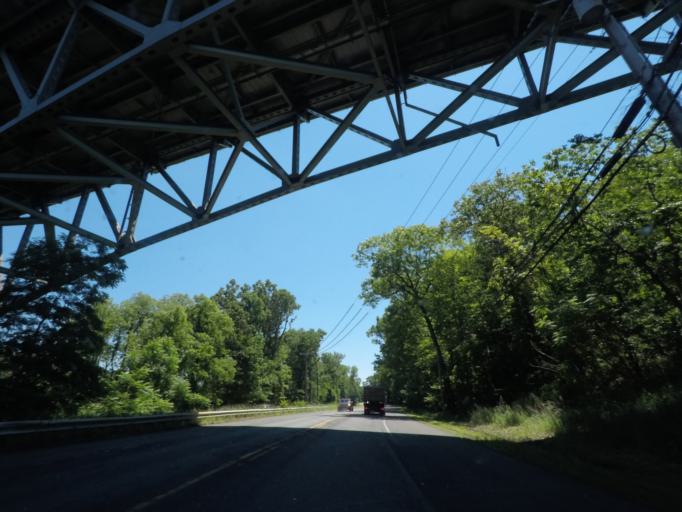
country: US
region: Massachusetts
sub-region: Hampden County
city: Westfield
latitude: 42.1569
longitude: -72.8150
